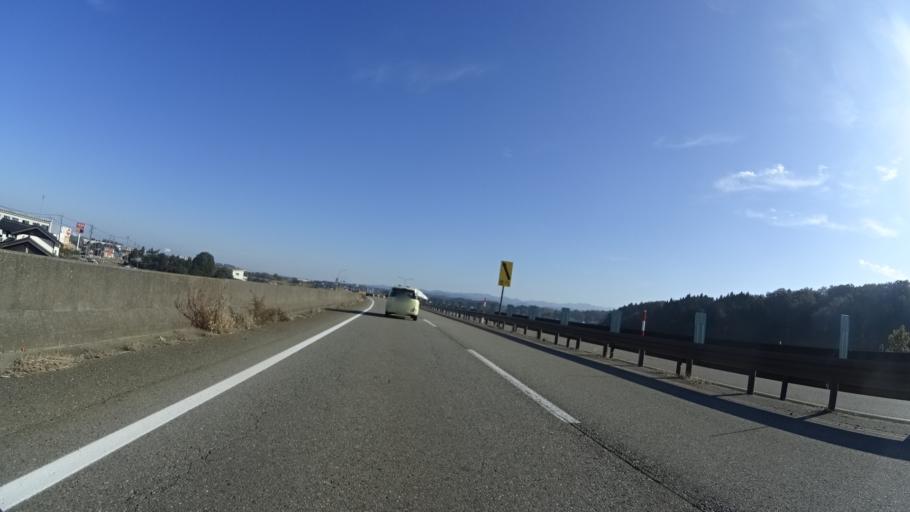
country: JP
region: Ishikawa
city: Komatsu
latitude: 36.3274
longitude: 136.4129
